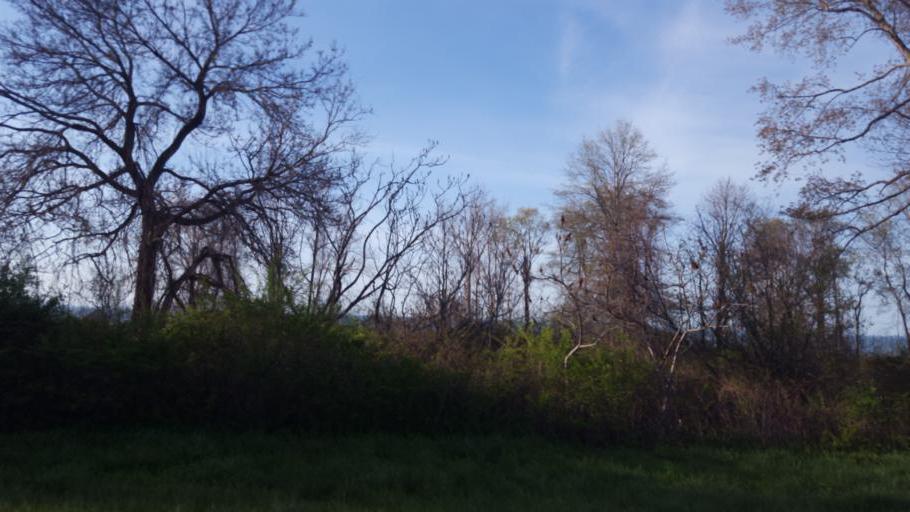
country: US
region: Ohio
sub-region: Ashtabula County
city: North Kingsville
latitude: 41.9170
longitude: -80.7323
